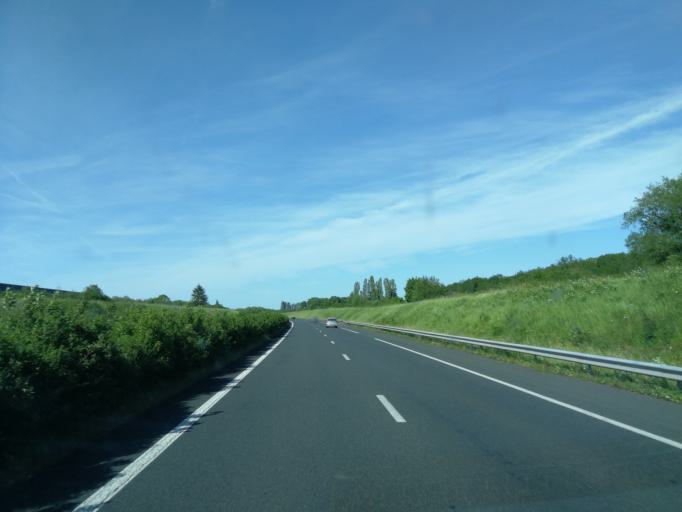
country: FR
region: Centre
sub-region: Departement d'Indre-et-Loire
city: Ballan-Mire
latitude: 47.3231
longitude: 0.6018
